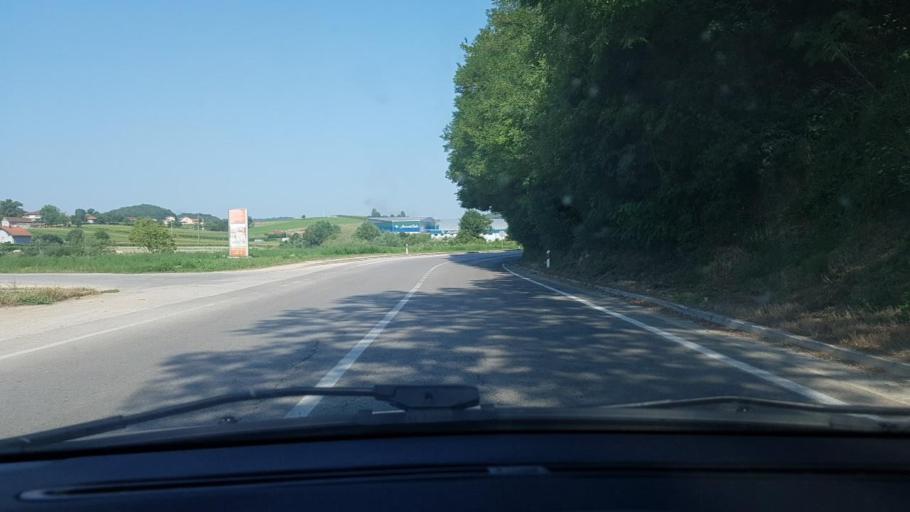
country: BA
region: Federation of Bosnia and Herzegovina
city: Velika Kladusa
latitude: 45.1576
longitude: 15.8250
